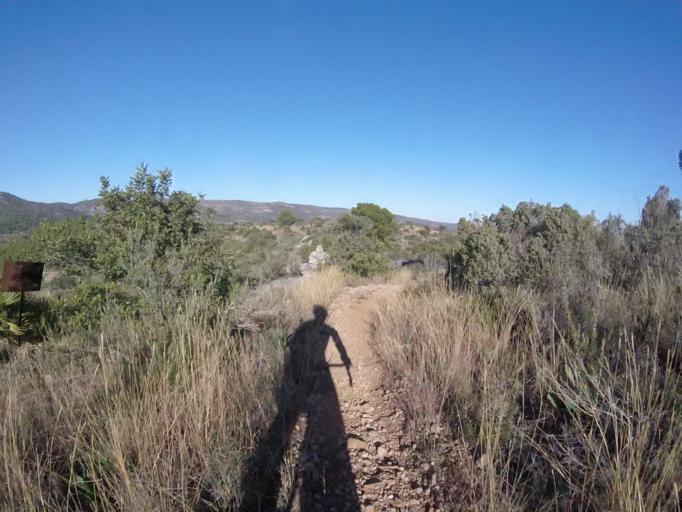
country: ES
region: Valencia
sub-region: Provincia de Castello
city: Orpesa/Oropesa del Mar
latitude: 40.1211
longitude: 0.1213
